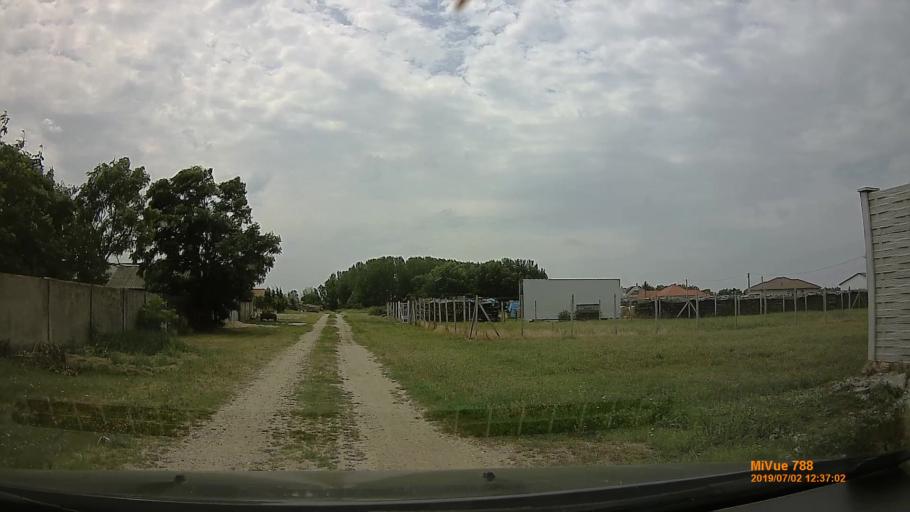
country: HU
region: Gyor-Moson-Sopron
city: Janossomorja
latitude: 47.8539
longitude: 17.1702
